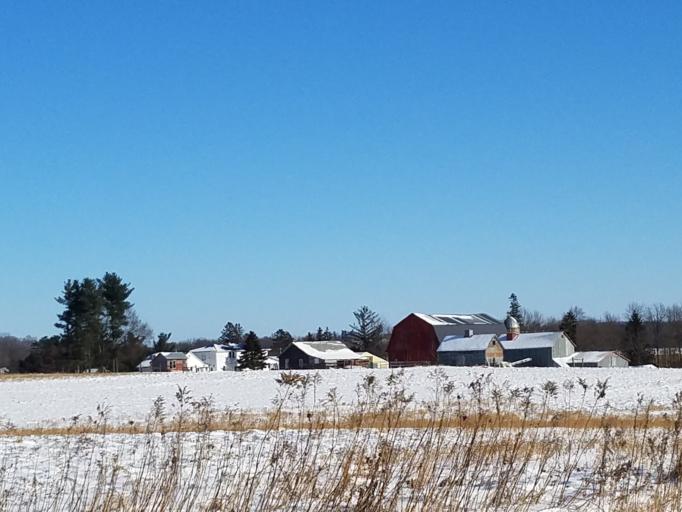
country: US
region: Wisconsin
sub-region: Clark County
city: Neillsville
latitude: 44.5675
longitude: -90.4216
